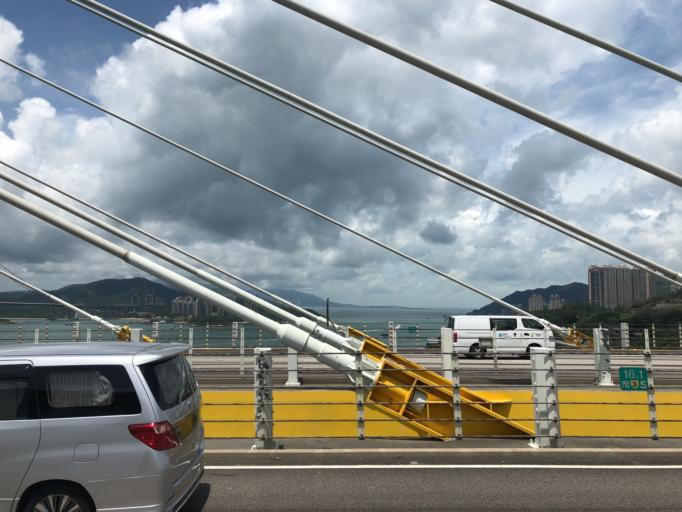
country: HK
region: Tsuen Wan
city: Tsuen Wan
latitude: 22.3663
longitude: 114.0787
